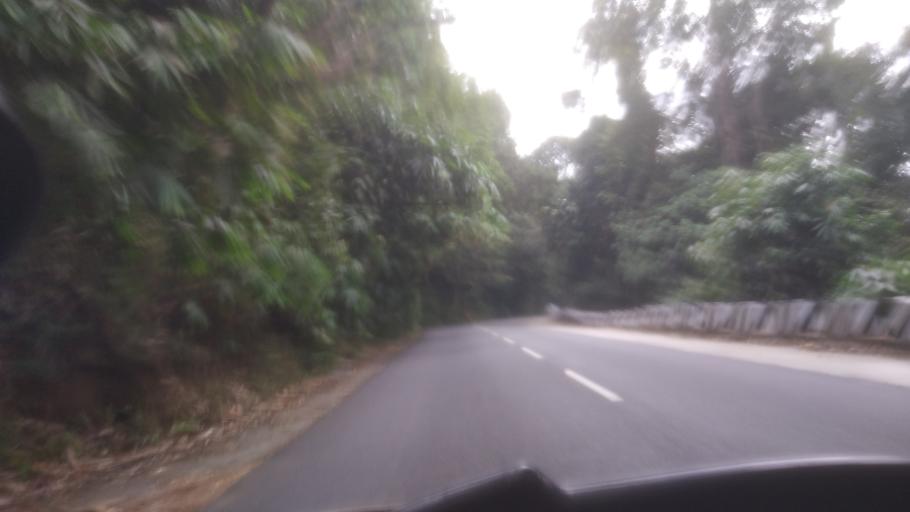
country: IN
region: Kerala
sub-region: Idukki
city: Kuttampuzha
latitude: 10.0573
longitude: 76.8042
